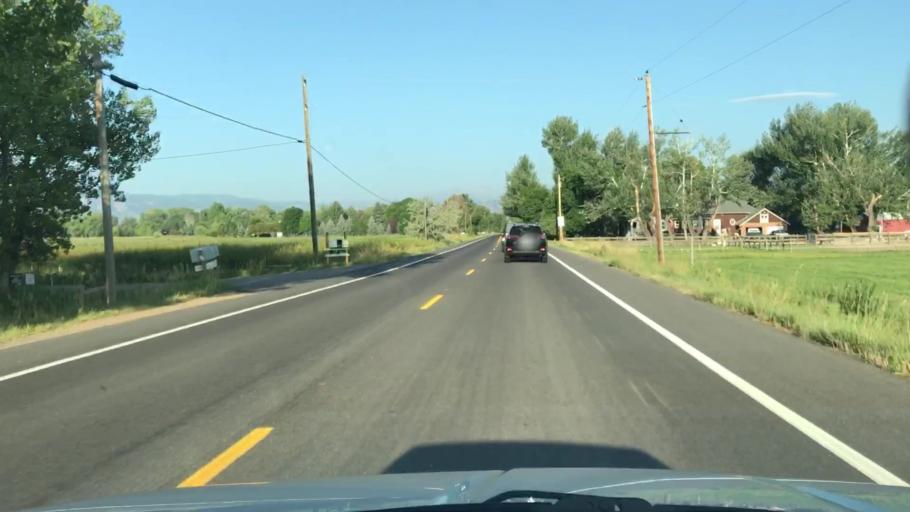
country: US
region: Colorado
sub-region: Boulder County
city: Gunbarrel
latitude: 40.0365
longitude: -105.1620
